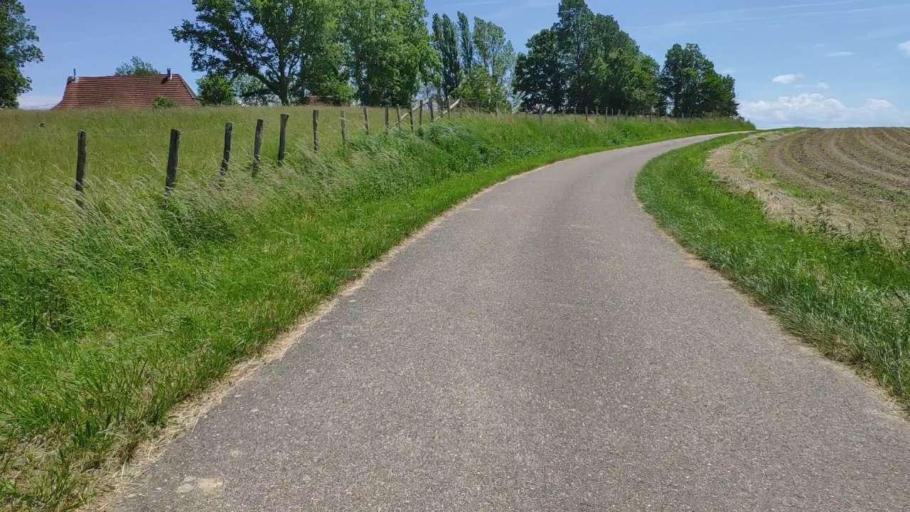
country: FR
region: Franche-Comte
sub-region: Departement du Jura
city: Bletterans
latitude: 46.7999
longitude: 5.3861
